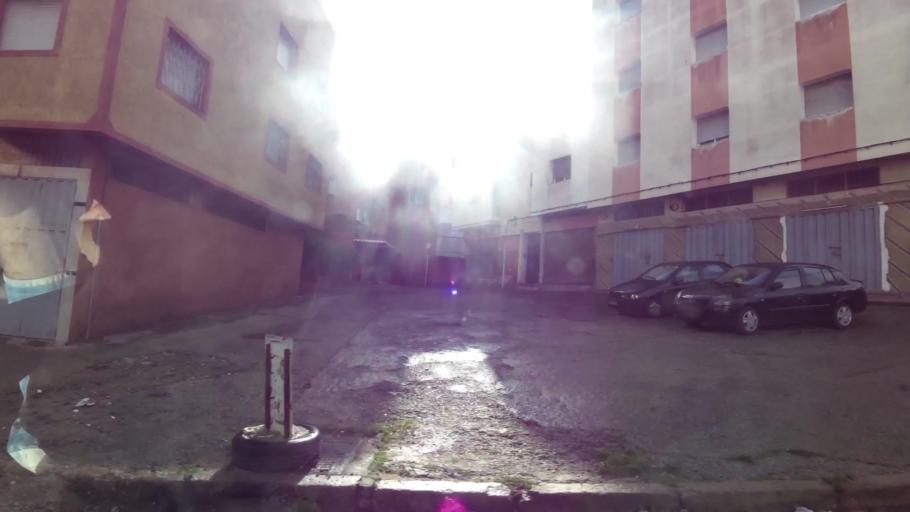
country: MA
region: Grand Casablanca
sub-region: Casablanca
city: Casablanca
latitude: 33.5563
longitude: -7.6856
